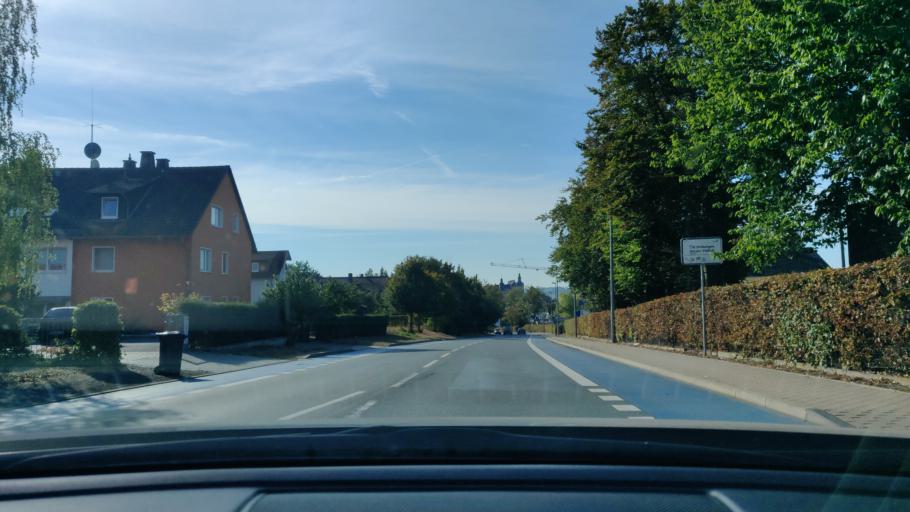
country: DE
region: Hesse
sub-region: Regierungsbezirk Kassel
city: Bad Wildungen
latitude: 51.1312
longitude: 9.1239
